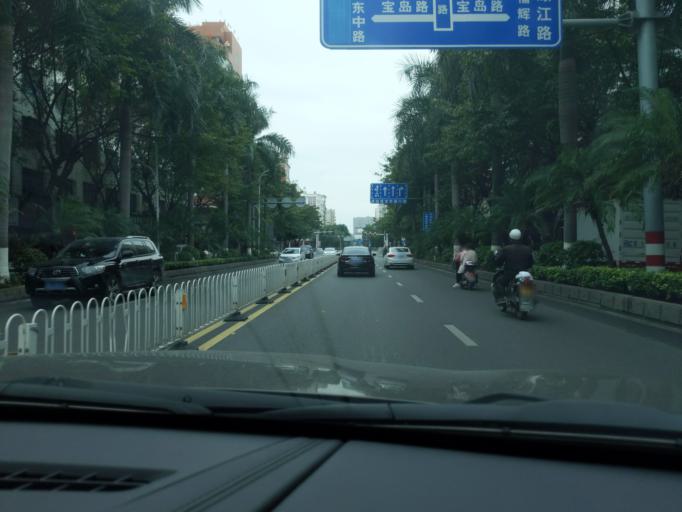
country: CN
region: Fujian
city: Shishi
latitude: 24.7374
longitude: 118.6399
